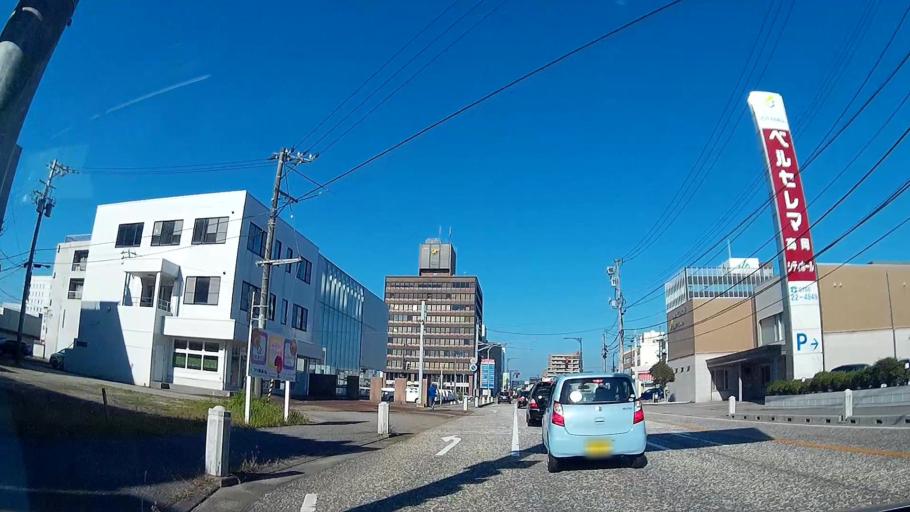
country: JP
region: Toyama
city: Takaoka
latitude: 36.7525
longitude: 137.0219
